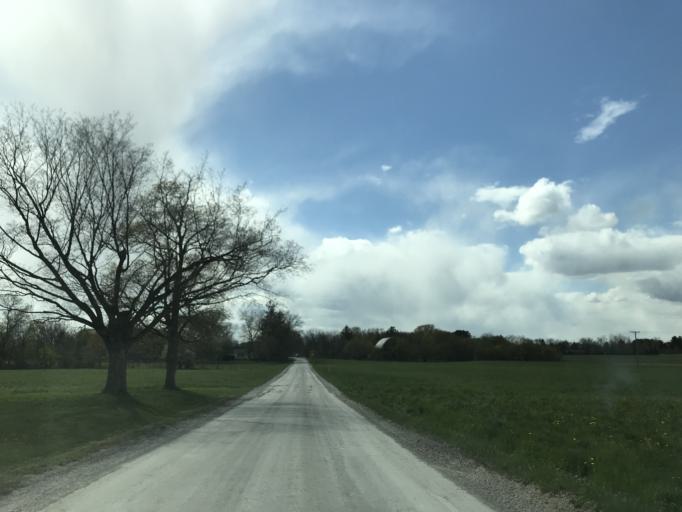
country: US
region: Michigan
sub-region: Oakland County
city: South Lyon
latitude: 42.3888
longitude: -83.6581
